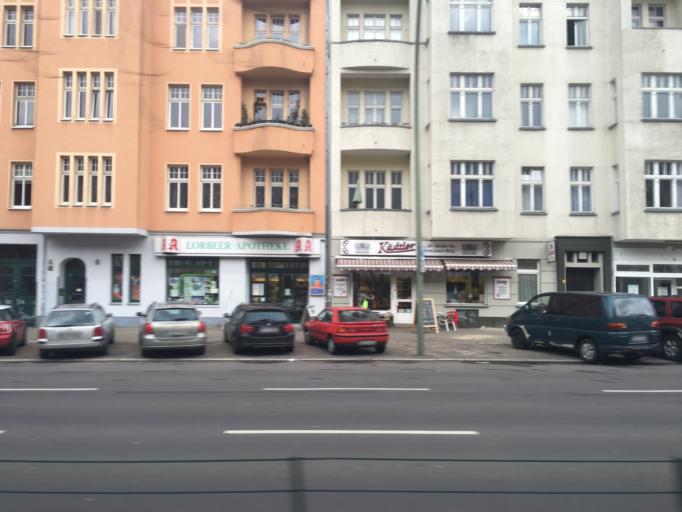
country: DE
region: Berlin
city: Prenzlauer Berg Bezirk
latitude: 52.5351
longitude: 13.4356
